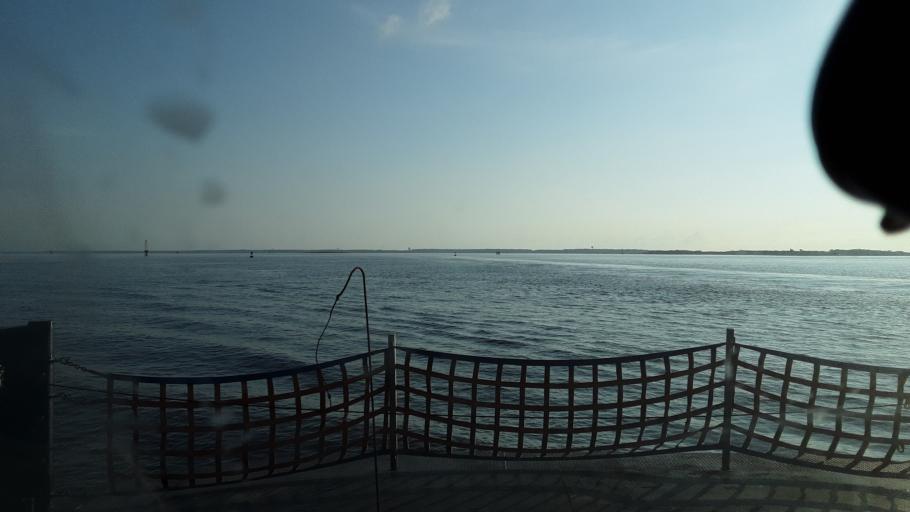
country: US
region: North Carolina
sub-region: New Hanover County
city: Kure Beach
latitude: 33.9553
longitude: -77.9587
